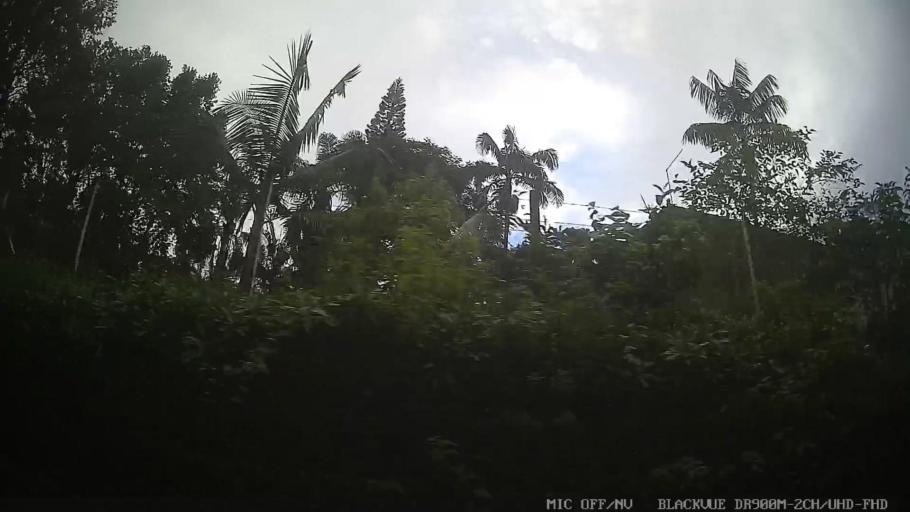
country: BR
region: Sao Paulo
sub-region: Rio Grande Da Serra
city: Rio Grande da Serra
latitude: -23.6888
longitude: -46.3108
